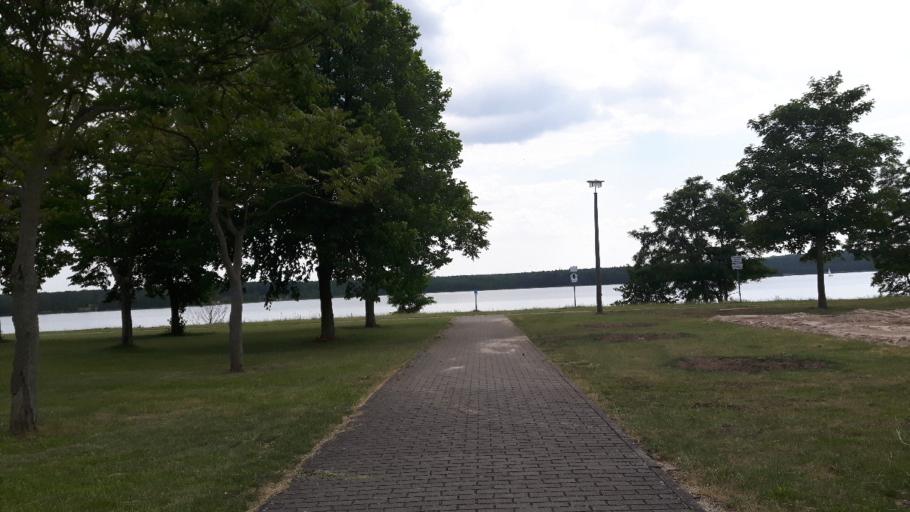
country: DE
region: Saxony-Anhalt
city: Bergwitz
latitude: 51.7930
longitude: 12.5774
